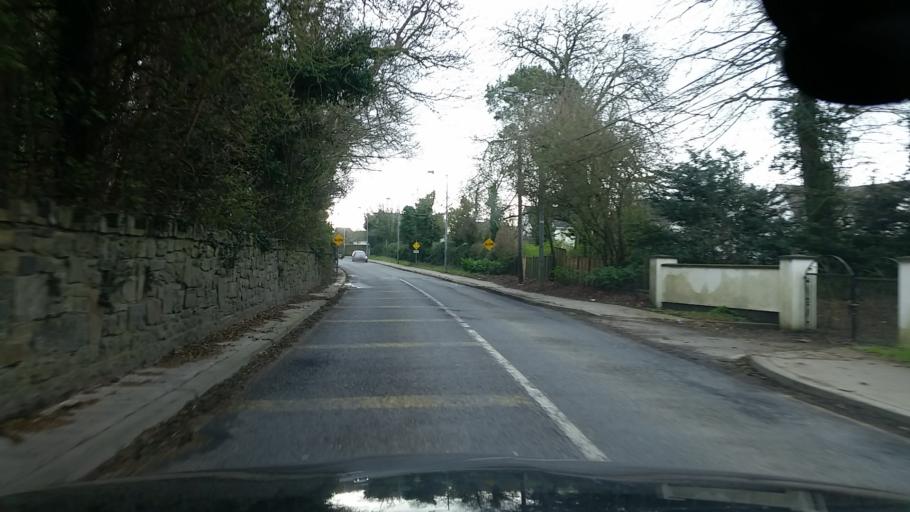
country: IE
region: Leinster
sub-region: Fingal County
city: Blanchardstown
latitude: 53.4282
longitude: -6.3733
